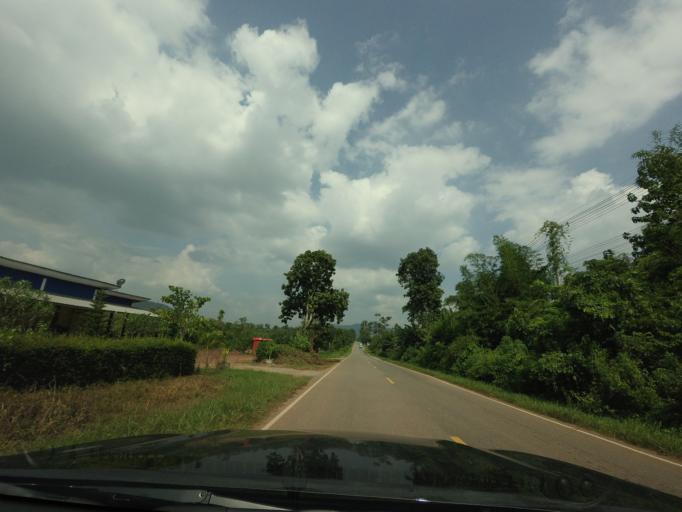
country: TH
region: Uttaradit
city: Ban Khok
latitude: 18.0336
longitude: 101.0903
